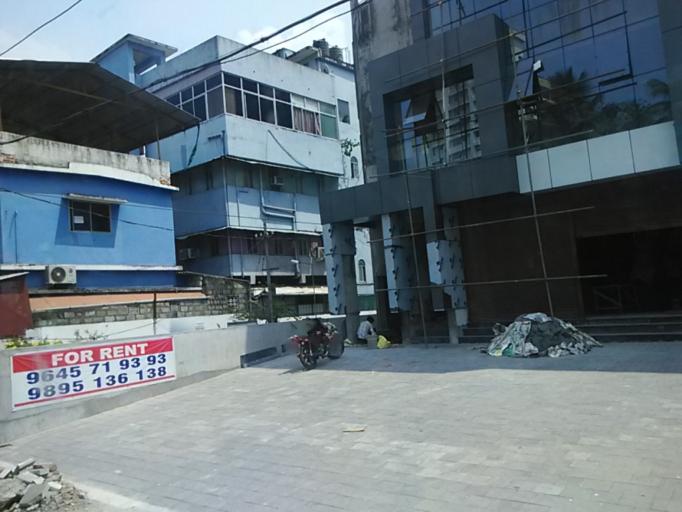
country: IN
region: Kerala
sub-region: Kozhikode
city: Kozhikode
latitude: 11.2671
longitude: 75.7769
